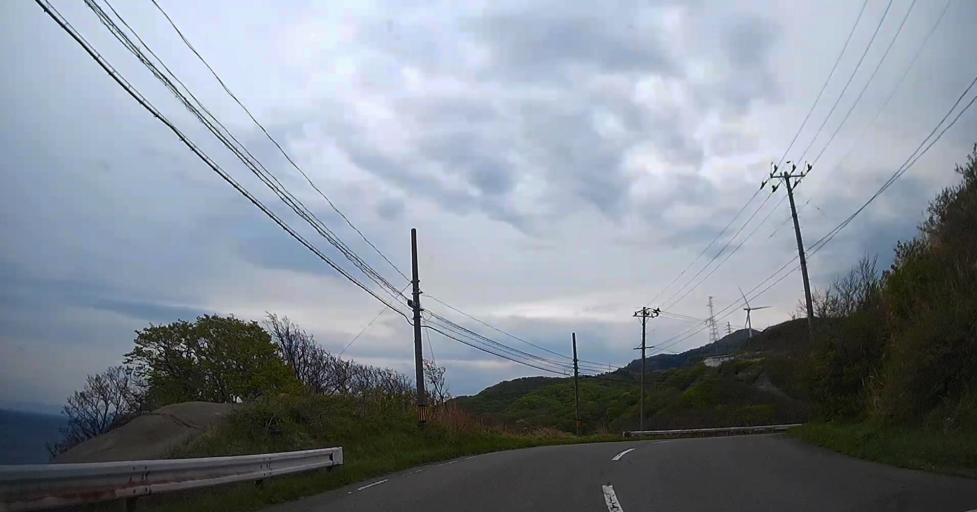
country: JP
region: Aomori
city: Shimokizukuri
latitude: 41.2563
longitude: 140.3493
